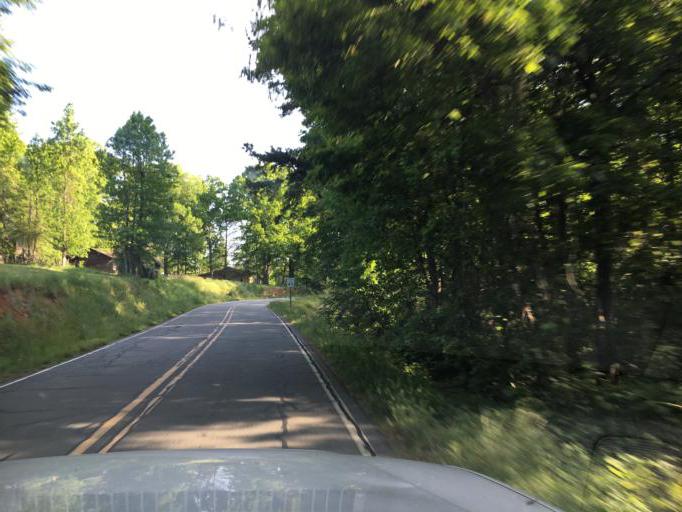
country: US
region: North Carolina
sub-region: Rutherford County
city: Rutherfordton
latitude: 35.3453
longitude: -81.9875
